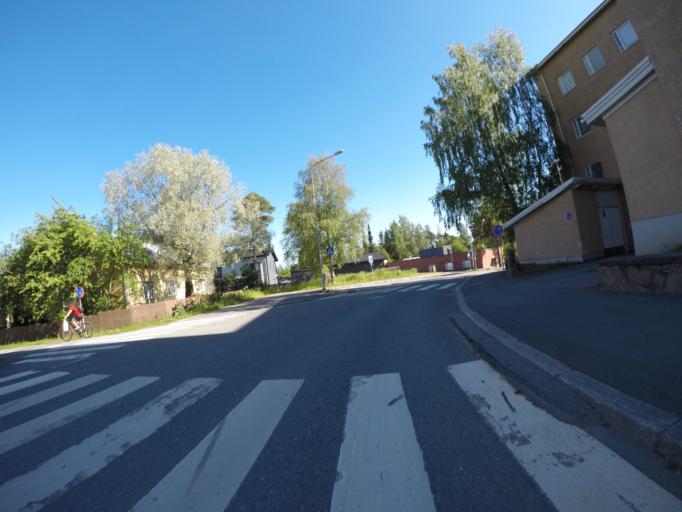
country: FI
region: Haeme
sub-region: Haemeenlinna
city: Haemeenlinna
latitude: 61.0055
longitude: 24.4845
